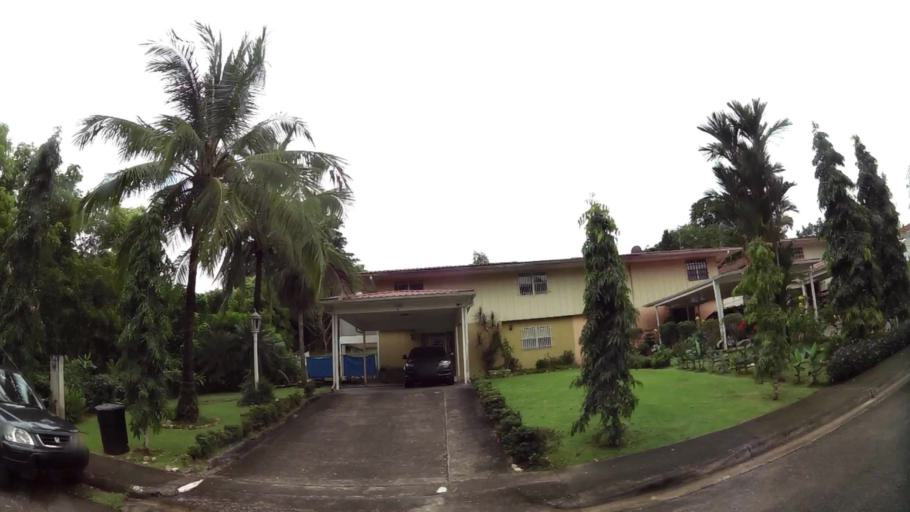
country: PA
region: Panama
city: Panama
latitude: 9.0059
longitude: -79.5621
